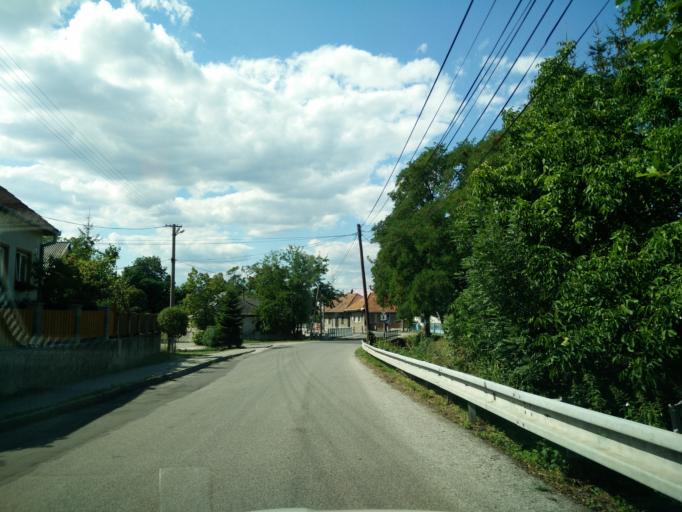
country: SK
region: Nitriansky
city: Prievidza
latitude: 48.7300
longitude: 18.6235
